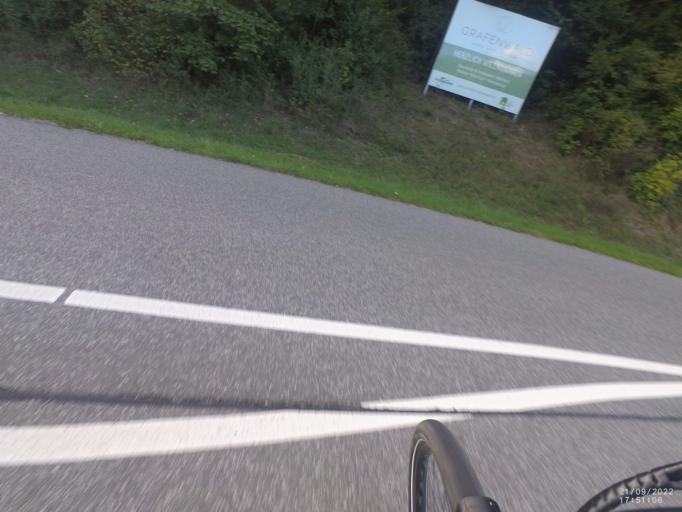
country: DE
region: Rheinland-Pfalz
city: Daun
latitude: 50.1768
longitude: 6.8266
